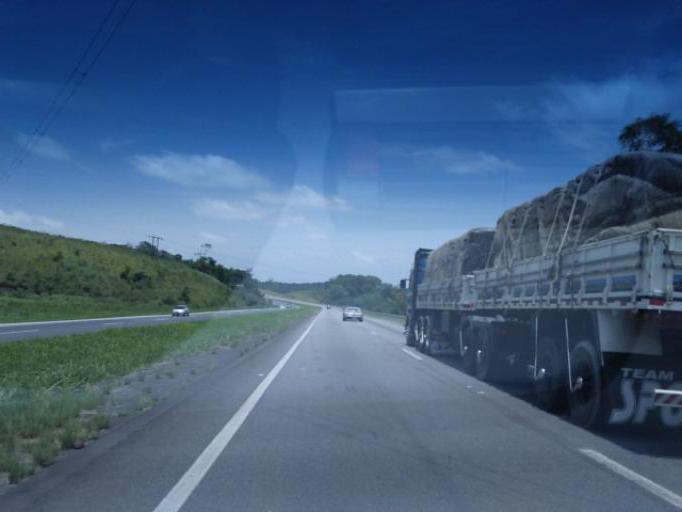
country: BR
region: Sao Paulo
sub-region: Miracatu
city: Miracatu
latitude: -24.2924
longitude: -47.4729
